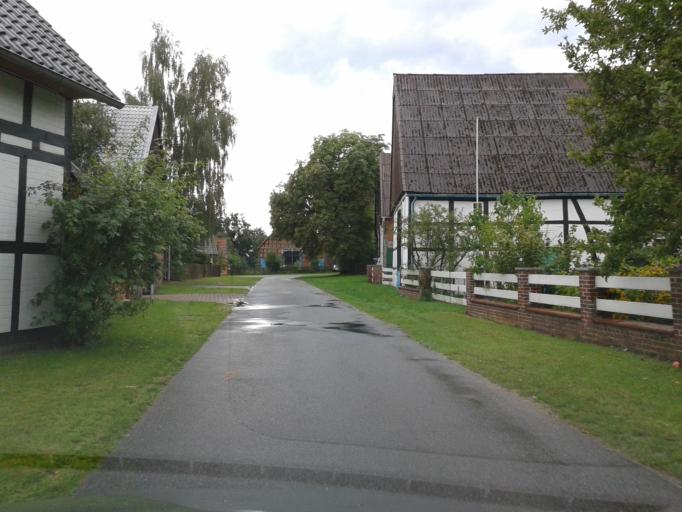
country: DE
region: Lower Saxony
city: Woltersdorf
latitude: 52.9351
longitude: 11.2613
